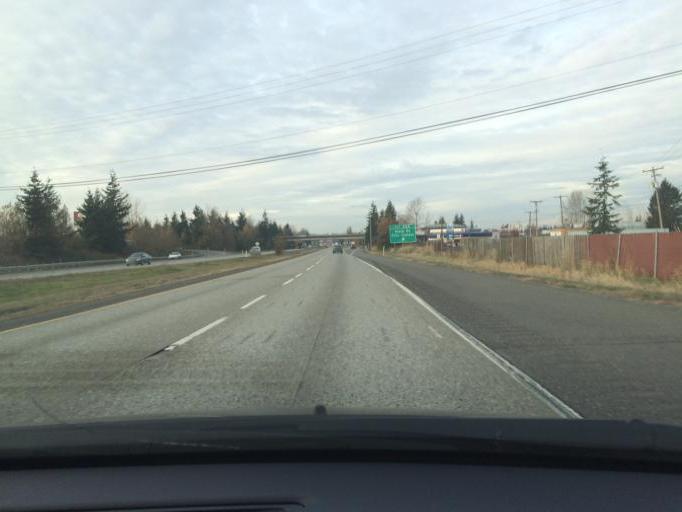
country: US
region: Washington
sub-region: Whatcom County
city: Ferndale
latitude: 48.8442
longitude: -122.5730
